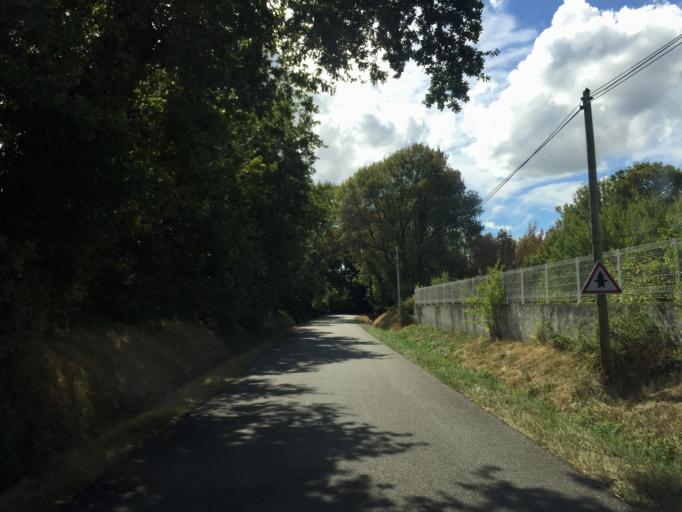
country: FR
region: Provence-Alpes-Cote d'Azur
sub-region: Departement du Vaucluse
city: Caderousse
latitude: 44.1040
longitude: 4.7627
